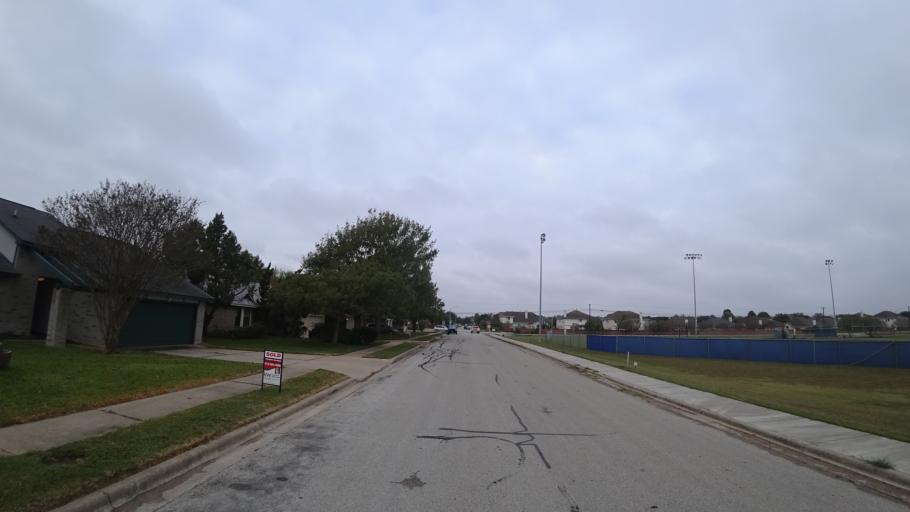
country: US
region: Texas
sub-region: Travis County
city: Pflugerville
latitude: 30.4261
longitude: -97.6150
